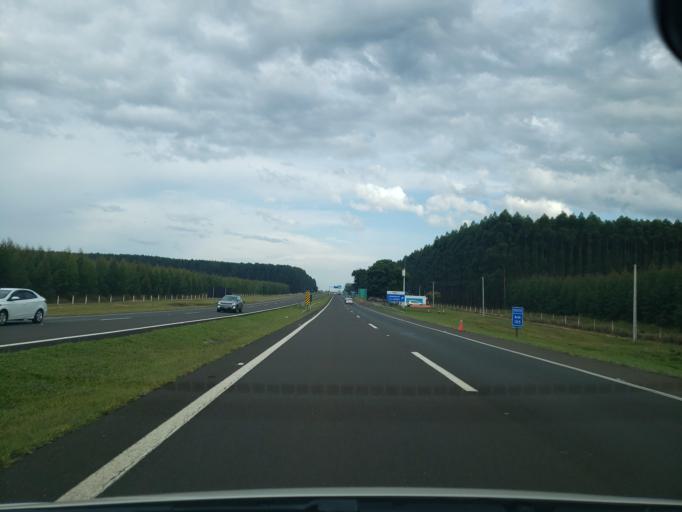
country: BR
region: Sao Paulo
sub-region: Itirapina
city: Itirapina
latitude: -22.2609
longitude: -47.8835
